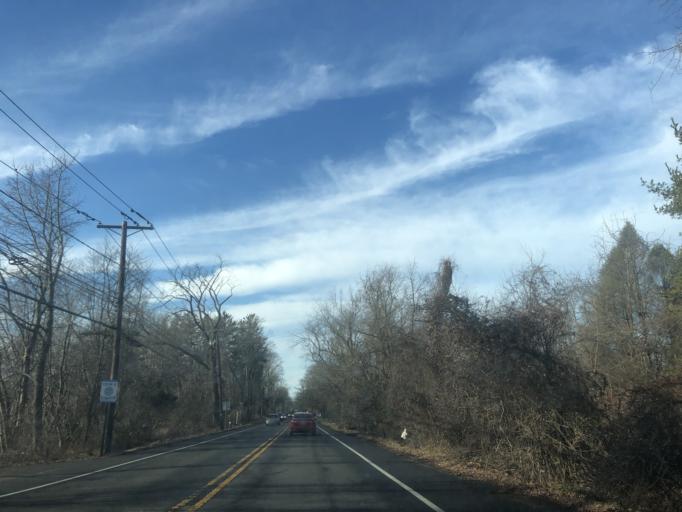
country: US
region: New Jersey
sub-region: Somerset County
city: Kingston
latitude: 40.3805
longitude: -74.6033
